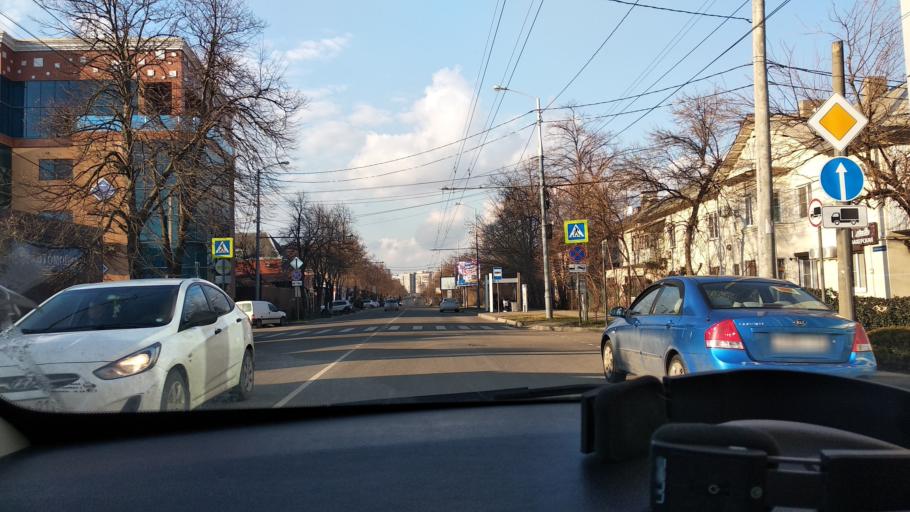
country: RU
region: Adygeya
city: Yablonovskiy
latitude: 45.0036
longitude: 38.9610
